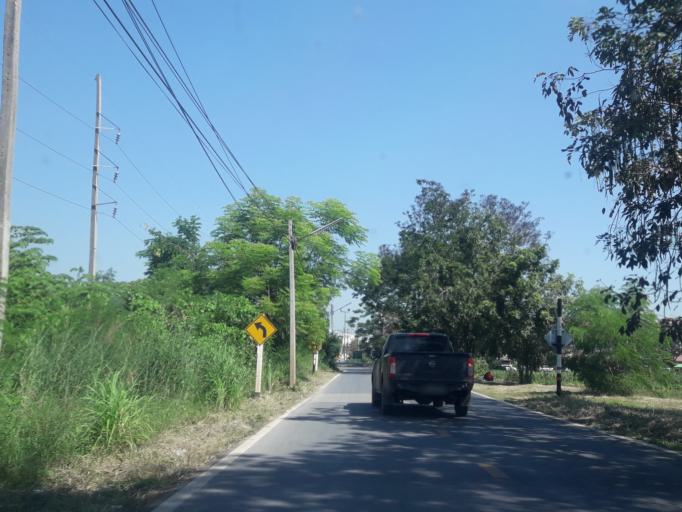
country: TH
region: Sara Buri
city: Nong Khae
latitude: 14.3319
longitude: 100.8731
